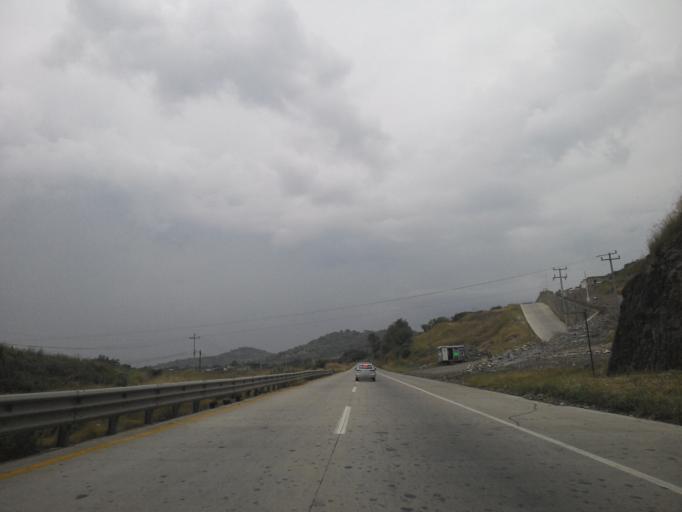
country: MX
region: Jalisco
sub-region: Tonala
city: Paseo Puente Viejo
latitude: 20.5747
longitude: -103.1739
